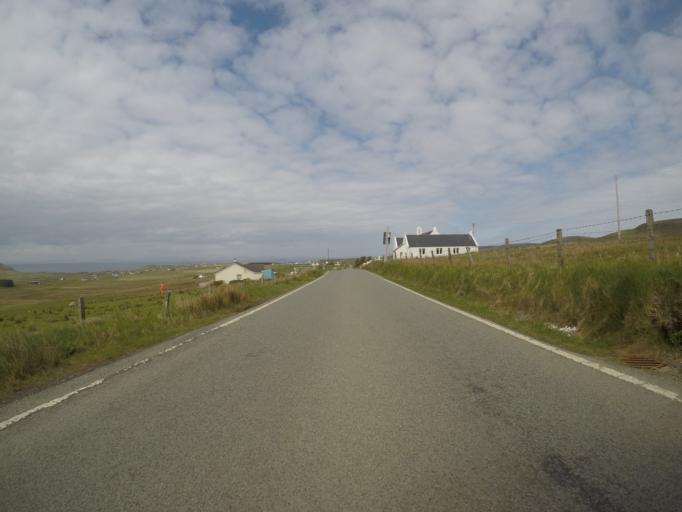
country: GB
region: Scotland
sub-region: Highland
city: Portree
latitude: 57.6376
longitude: -6.3763
